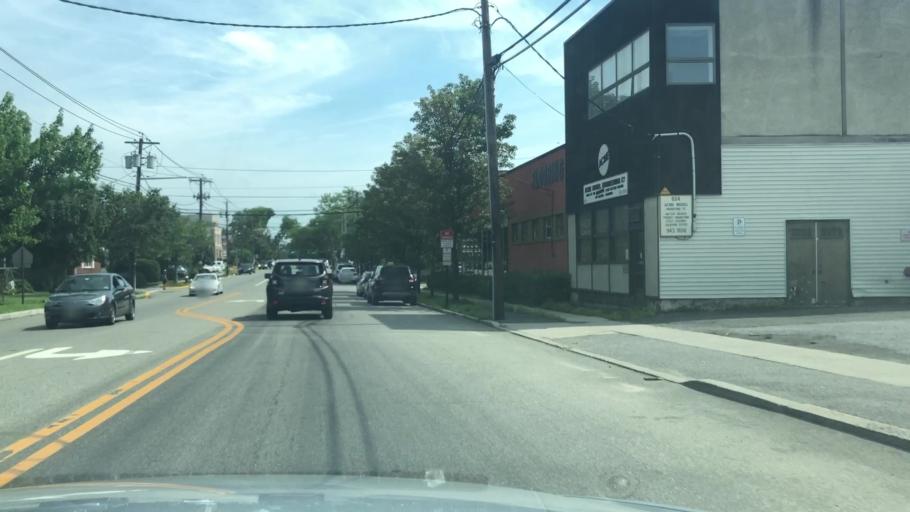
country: US
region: New Jersey
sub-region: Bergen County
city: Cliffside Park
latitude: 40.8297
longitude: -73.9934
